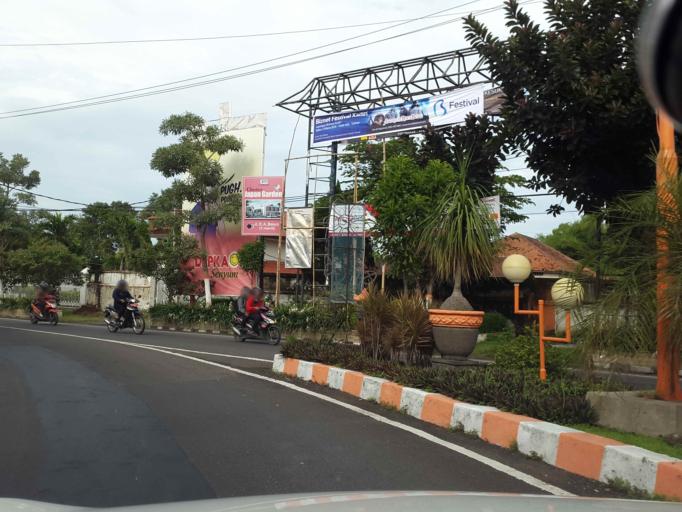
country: ID
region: East Java
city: Soko
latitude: -7.4812
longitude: 112.4290
